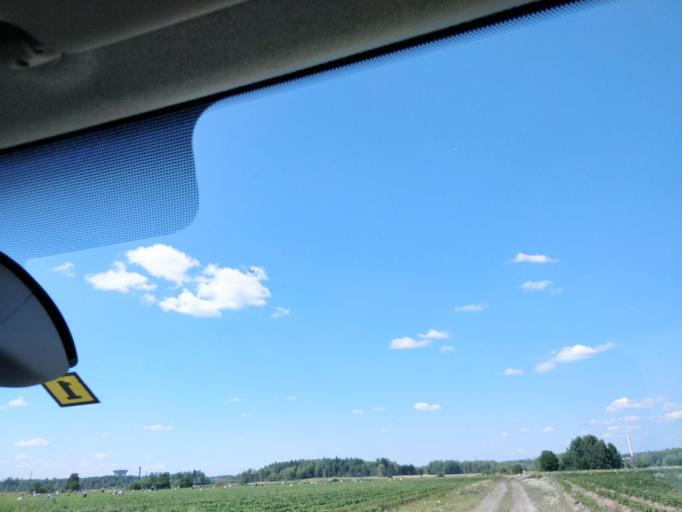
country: FI
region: Uusimaa
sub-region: Helsinki
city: Vantaa
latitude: 60.3070
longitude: 25.0749
